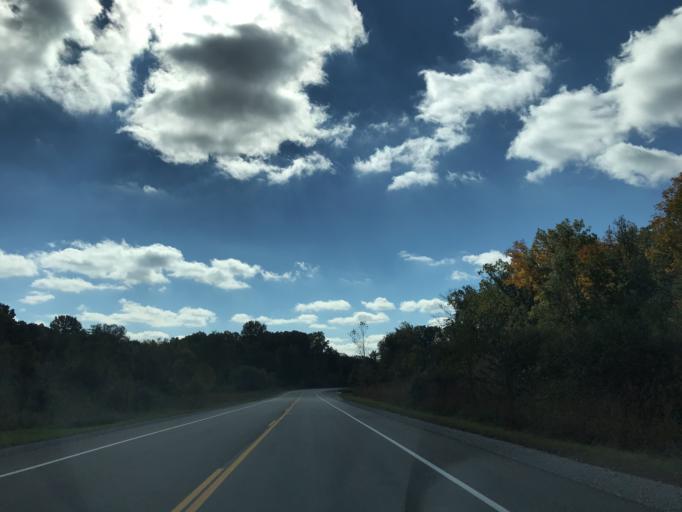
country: US
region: Michigan
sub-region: Washtenaw County
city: Ann Arbor
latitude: 42.3057
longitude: -83.6770
